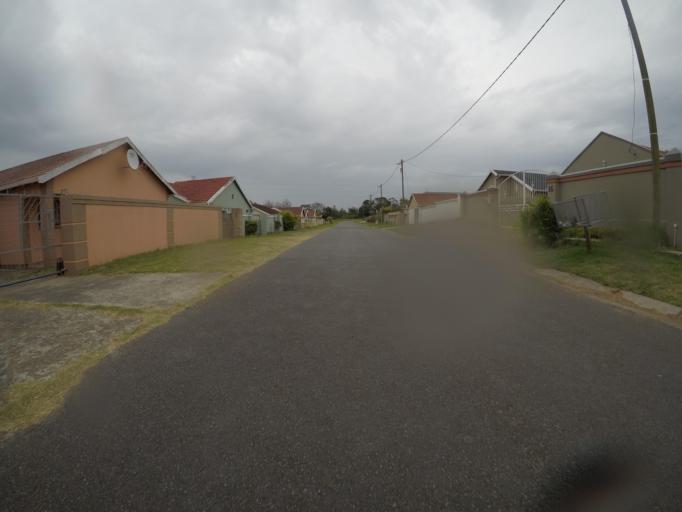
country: ZA
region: Eastern Cape
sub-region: Buffalo City Metropolitan Municipality
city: East London
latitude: -32.9885
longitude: 27.8453
